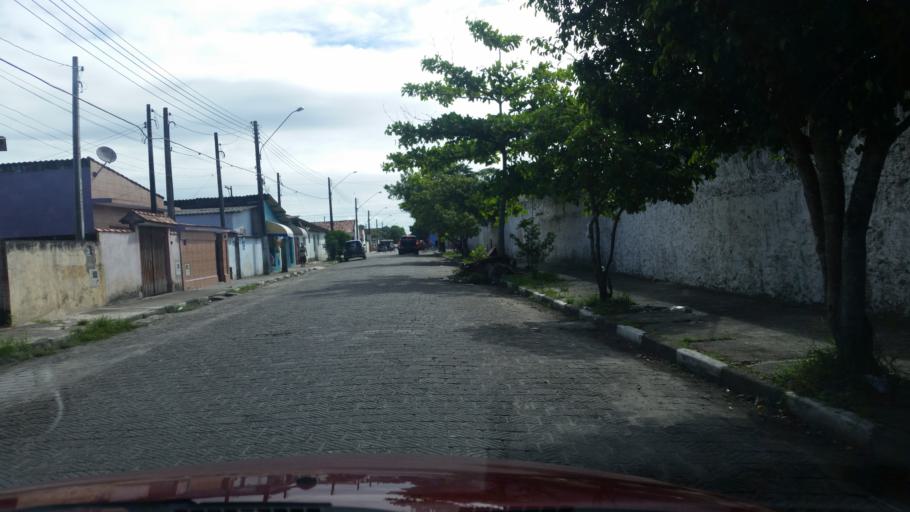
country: BR
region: Sao Paulo
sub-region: Iguape
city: Iguape
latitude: -24.7046
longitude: -47.5582
